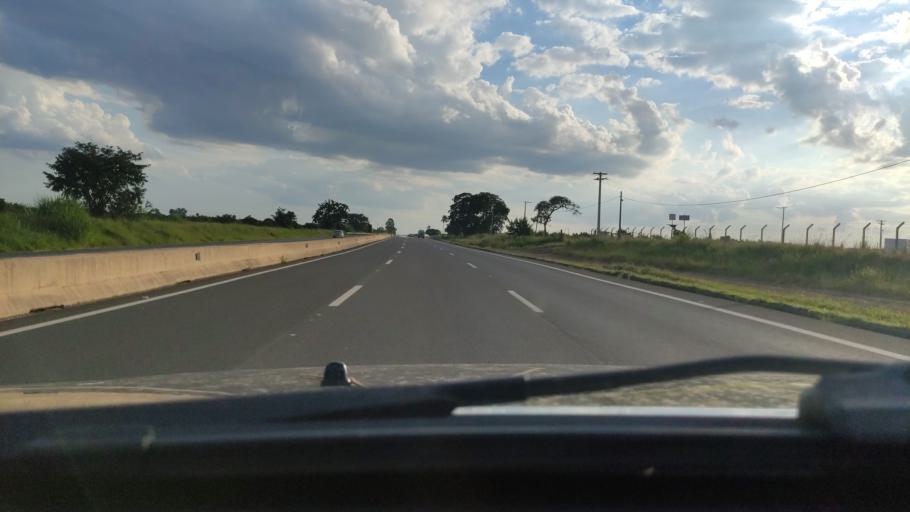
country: BR
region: Sao Paulo
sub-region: Mogi-Mirim
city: Mogi Mirim
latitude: -22.4518
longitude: -47.0863
